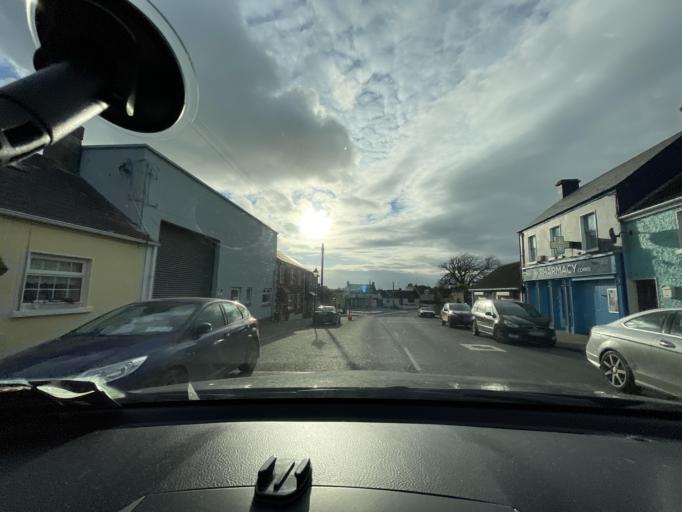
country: IE
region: Leinster
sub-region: Lu
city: Clogherhead
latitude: 53.7915
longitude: -6.2389
